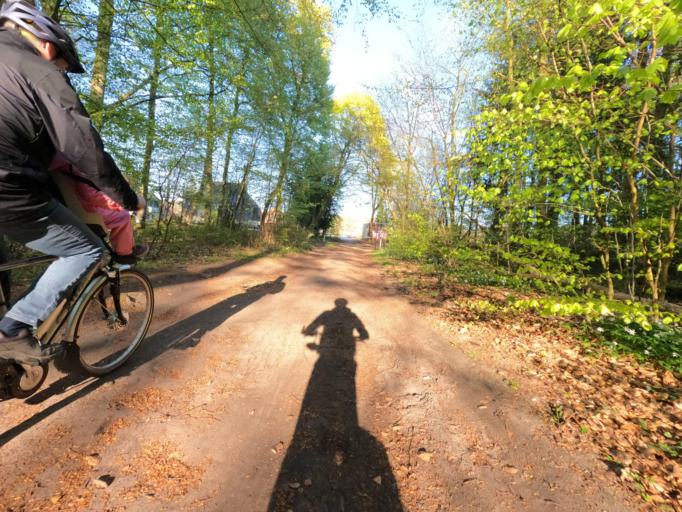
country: DE
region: Mecklenburg-Vorpommern
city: Ostseebad Prerow
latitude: 54.4418
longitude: 12.5446
